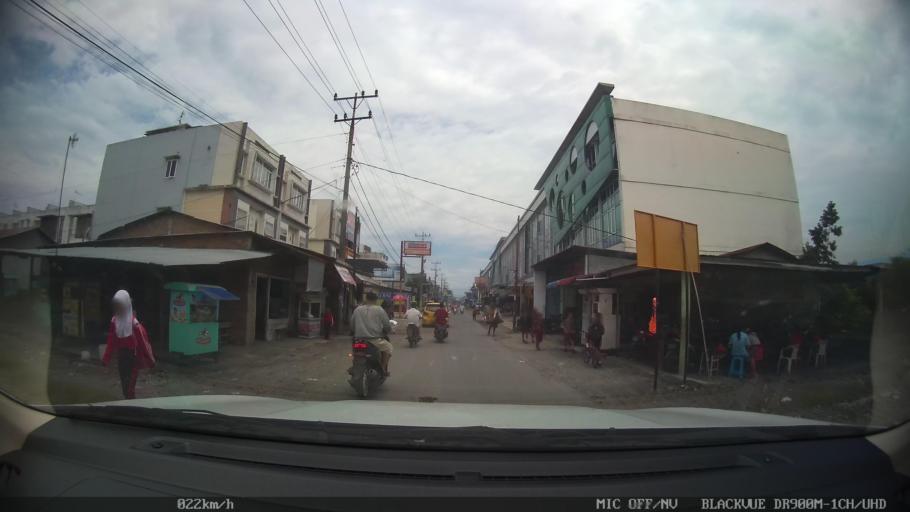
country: ID
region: North Sumatra
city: Sunggal
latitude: 3.6058
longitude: 98.5800
